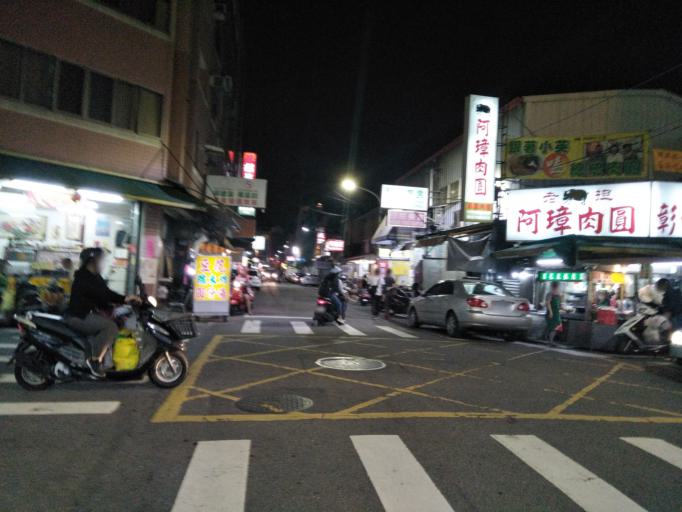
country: TW
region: Taiwan
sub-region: Changhua
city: Chang-hua
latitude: 24.0795
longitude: 120.5394
